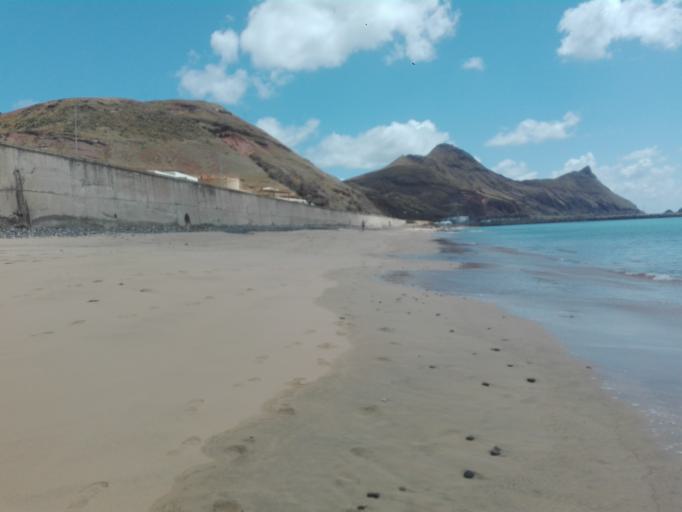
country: PT
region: Madeira
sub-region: Porto Santo
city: Vila de Porto Santo
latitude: 33.0623
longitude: -16.3237
